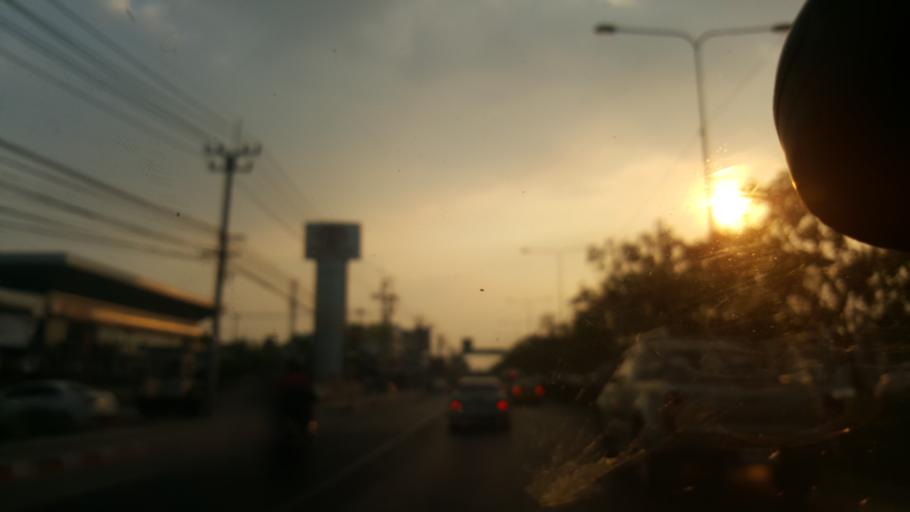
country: TH
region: Bangkok
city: Phasi Charoen
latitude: 13.7018
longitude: 100.4444
